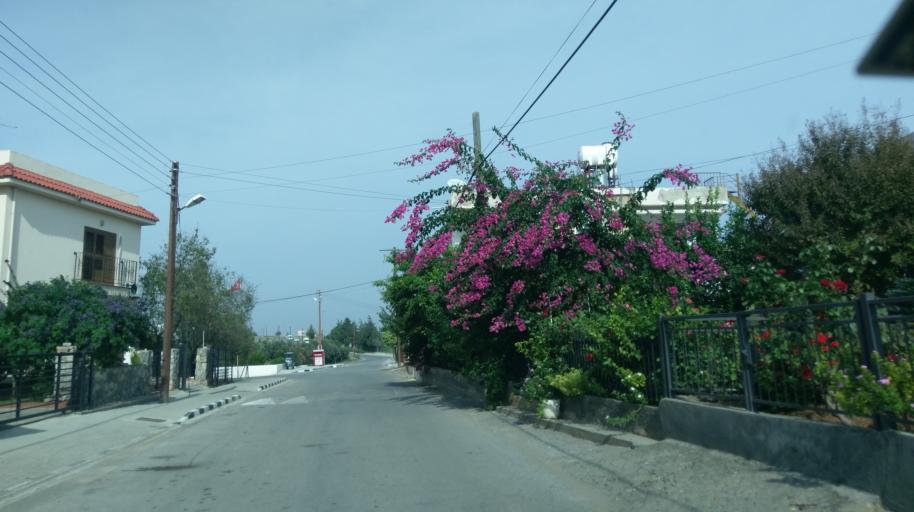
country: CY
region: Lefkosia
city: Morfou
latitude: 35.2468
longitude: 33.0379
